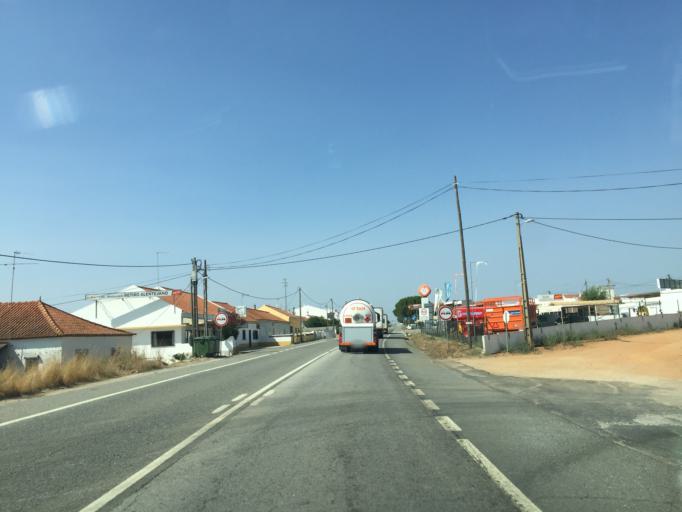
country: PT
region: Beja
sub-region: Aljustrel
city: Aljustrel
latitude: 37.9450
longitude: -8.3805
